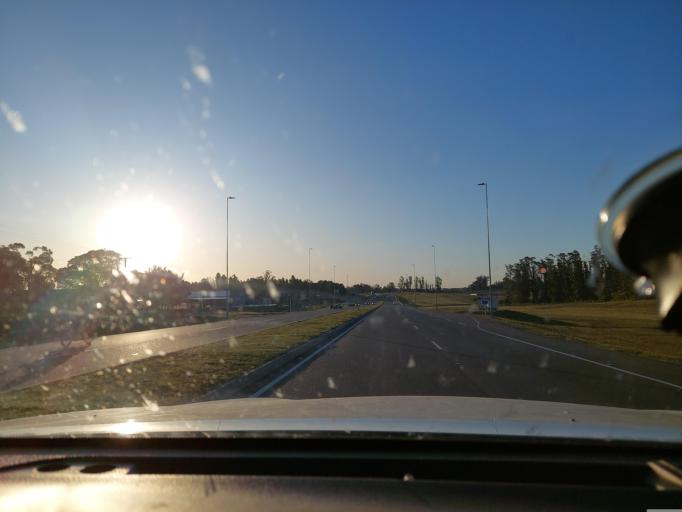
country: UY
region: Canelones
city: Empalme Olmos
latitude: -34.7007
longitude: -55.9098
